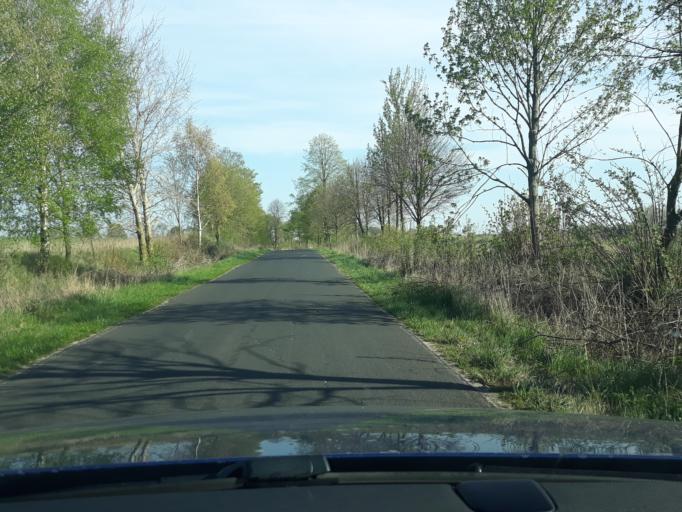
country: PL
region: Pomeranian Voivodeship
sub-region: Powiat czluchowski
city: Przechlewo
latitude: 53.8523
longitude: 17.3529
